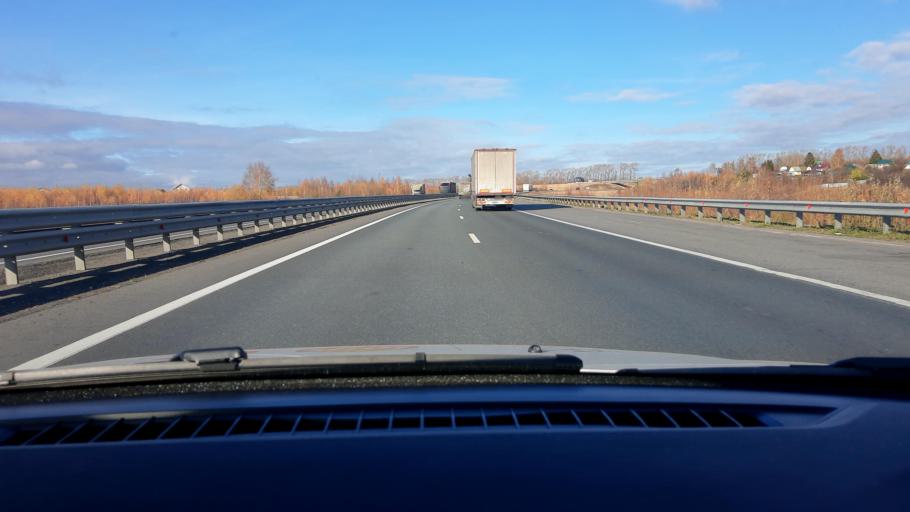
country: RU
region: Nizjnij Novgorod
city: Burevestnik
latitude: 56.1452
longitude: 43.7550
